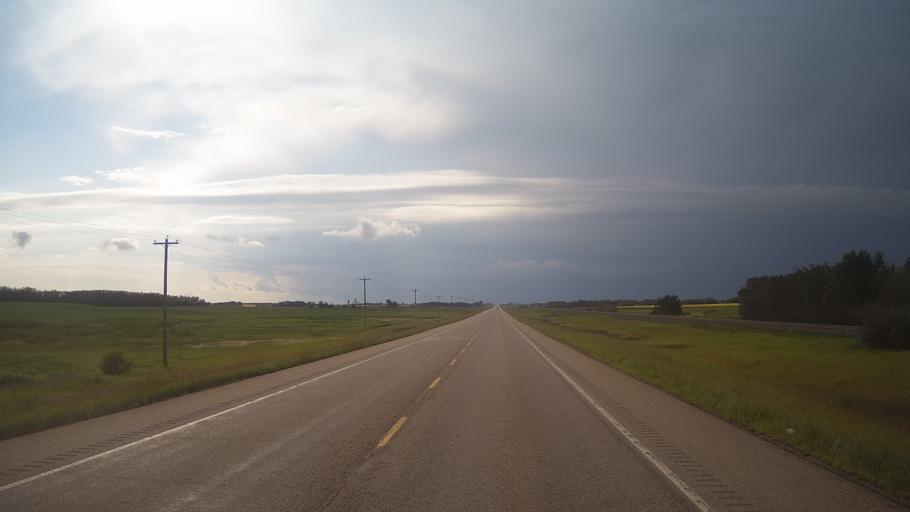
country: CA
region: Alberta
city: Viking
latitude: 53.1798
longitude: -112.0681
